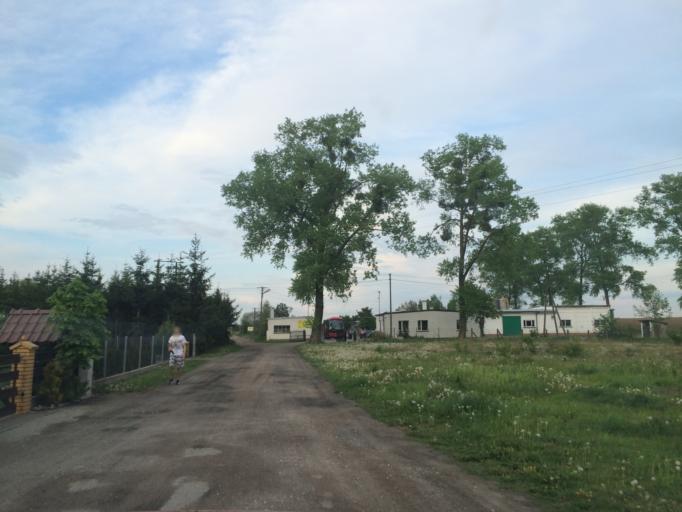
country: PL
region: Kujawsko-Pomorskie
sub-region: Powiat brodnicki
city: Brodnica
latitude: 53.3255
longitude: 19.4842
